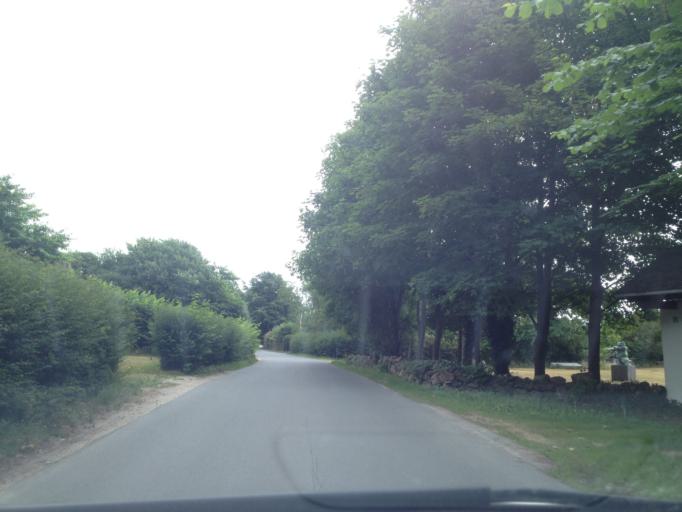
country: DK
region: Central Jutland
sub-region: Syddjurs Kommune
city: Ebeltoft
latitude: 56.1550
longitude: 10.6933
